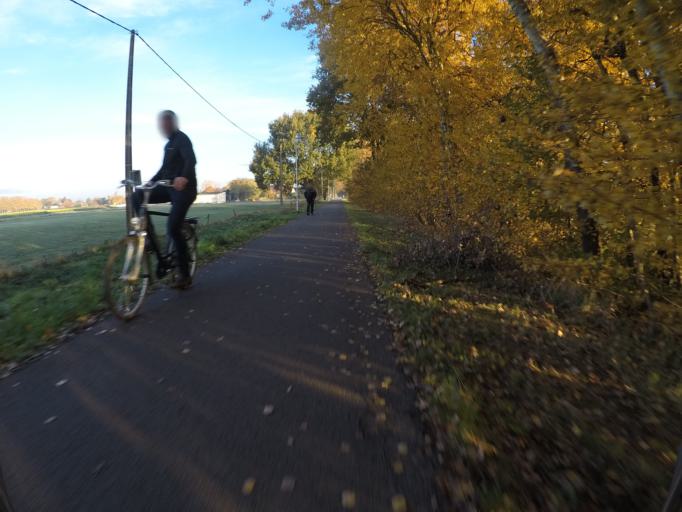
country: BE
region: Flanders
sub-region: Provincie Antwerpen
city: Olen
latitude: 51.1125
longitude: 4.8255
